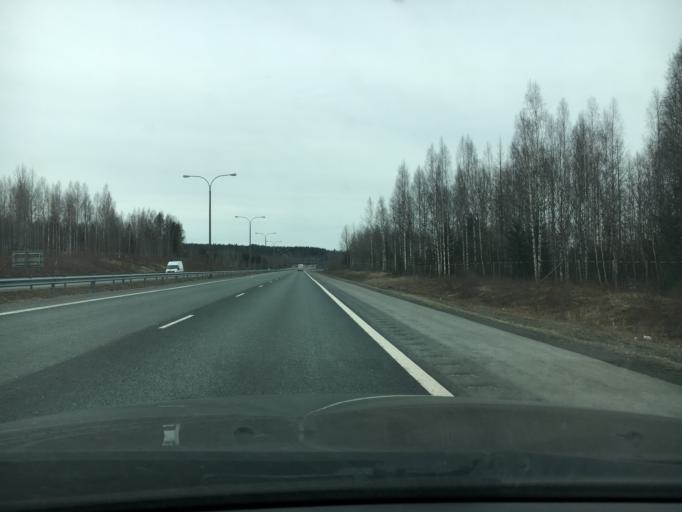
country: FI
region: Northern Savo
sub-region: Kuopio
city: Kuopio
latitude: 62.7910
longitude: 27.5944
